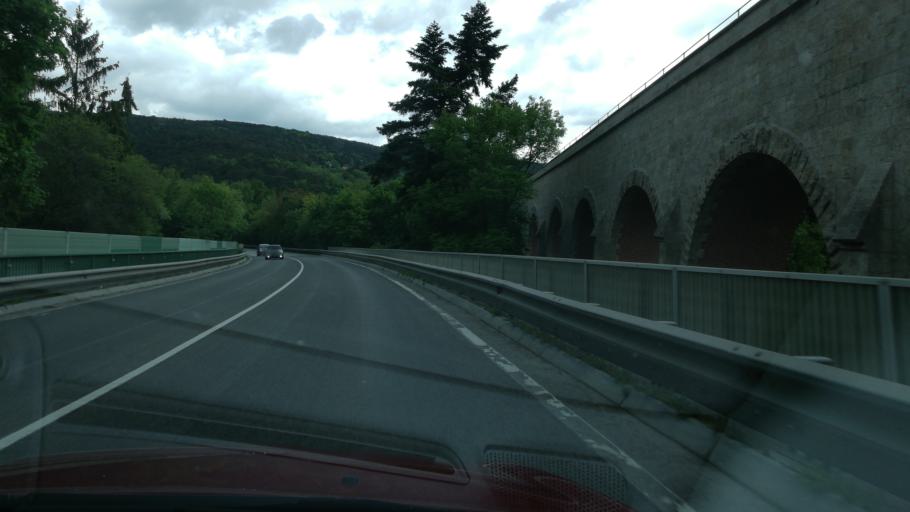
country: AT
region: Lower Austria
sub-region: Politischer Bezirk Baden
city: Baden
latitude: 48.0044
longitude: 16.2119
